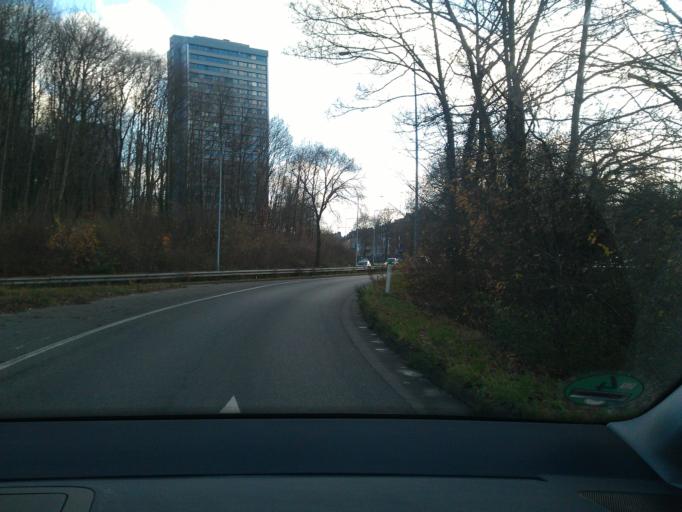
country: DE
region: North Rhine-Westphalia
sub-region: Regierungsbezirk Koln
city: Aachen
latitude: 50.7894
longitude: 6.0675
